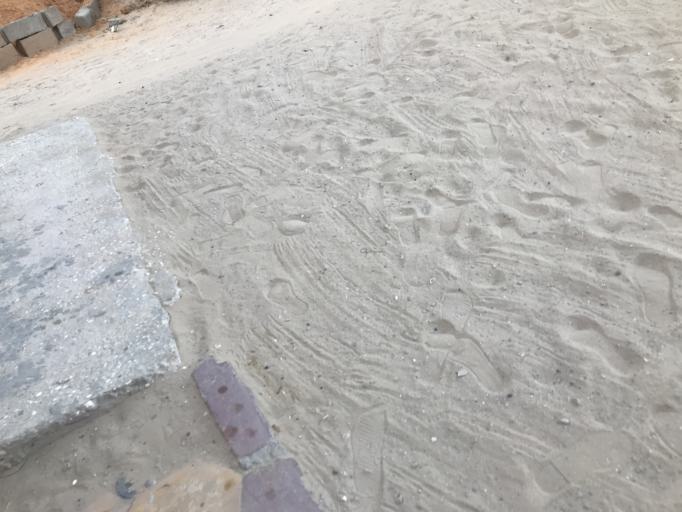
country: SN
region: Saint-Louis
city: Saint-Louis
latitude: 16.0385
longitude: -16.4468
